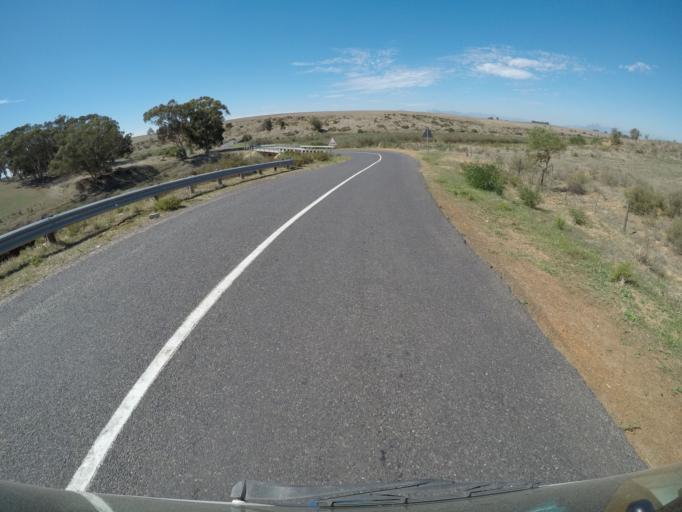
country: ZA
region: Western Cape
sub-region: City of Cape Town
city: Atlantis
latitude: -33.6779
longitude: 18.6042
